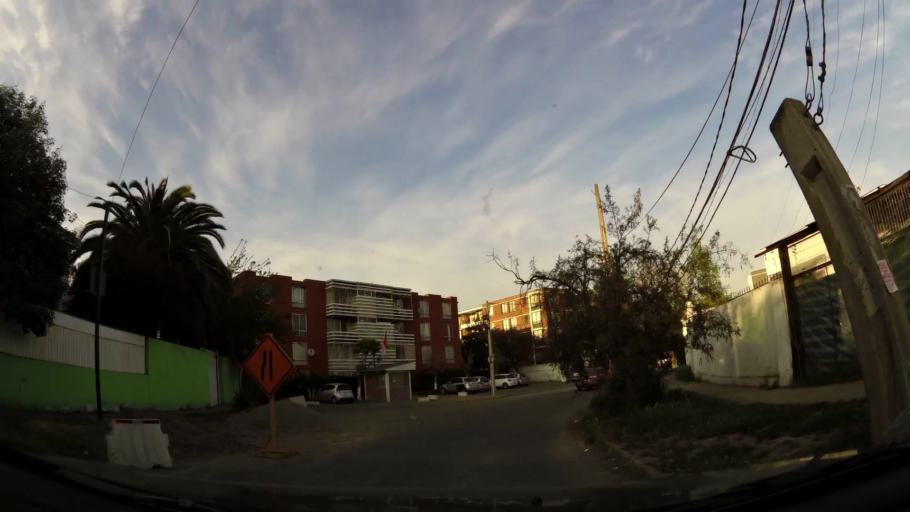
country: CL
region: Santiago Metropolitan
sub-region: Provincia de Santiago
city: Villa Presidente Frei, Nunoa, Santiago, Chile
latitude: -33.4567
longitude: -70.5770
